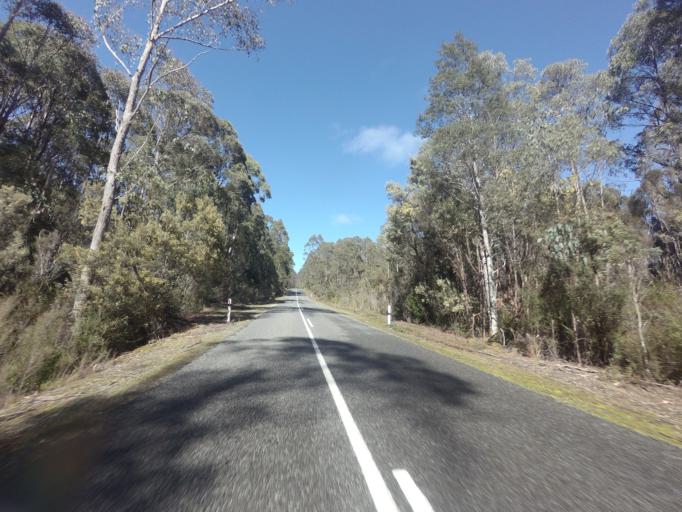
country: AU
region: Tasmania
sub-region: Derwent Valley
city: New Norfolk
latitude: -42.7401
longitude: 146.4198
